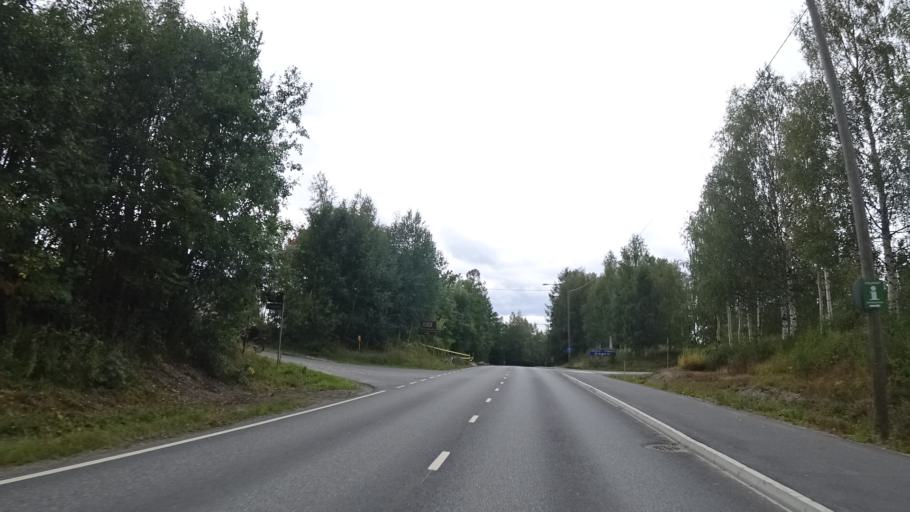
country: FI
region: North Karelia
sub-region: Joensuu
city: Ilomantsi
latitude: 62.6547
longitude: 30.9426
